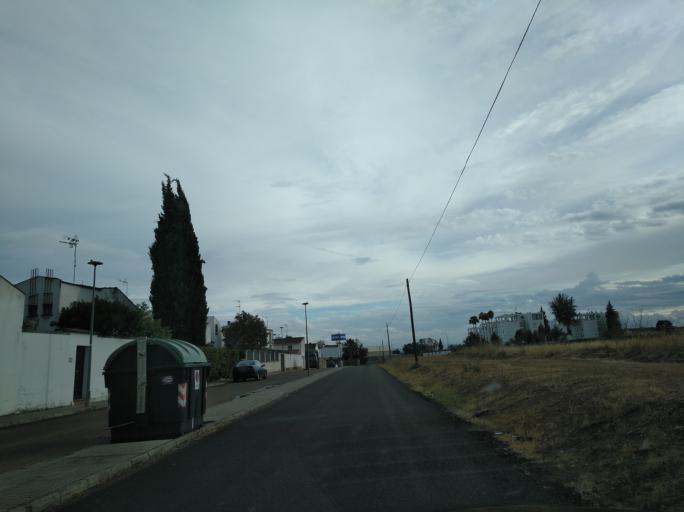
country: ES
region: Extremadura
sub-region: Provincia de Badajoz
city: Badajoz
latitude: 38.8854
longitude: -7.0138
